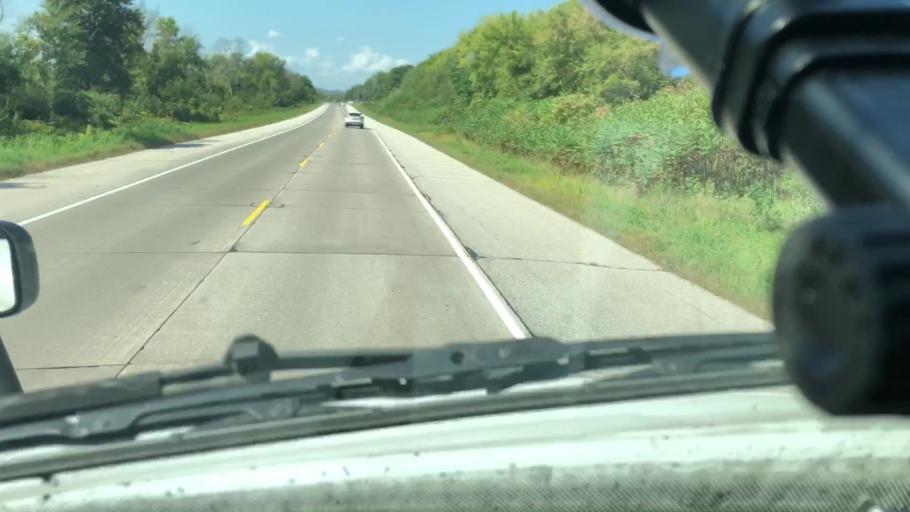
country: US
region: Minnesota
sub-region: Winona County
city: Winona
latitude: 44.0705
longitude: -91.6091
